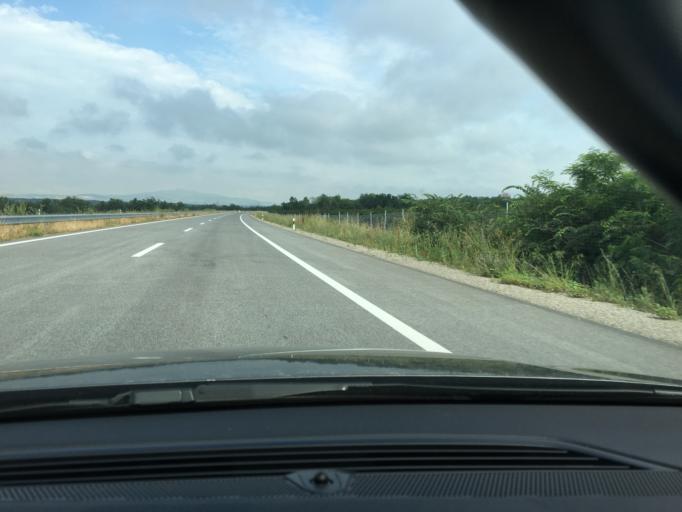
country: MK
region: Sveti Nikole
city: Sveti Nikole
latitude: 41.8314
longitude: 21.9942
